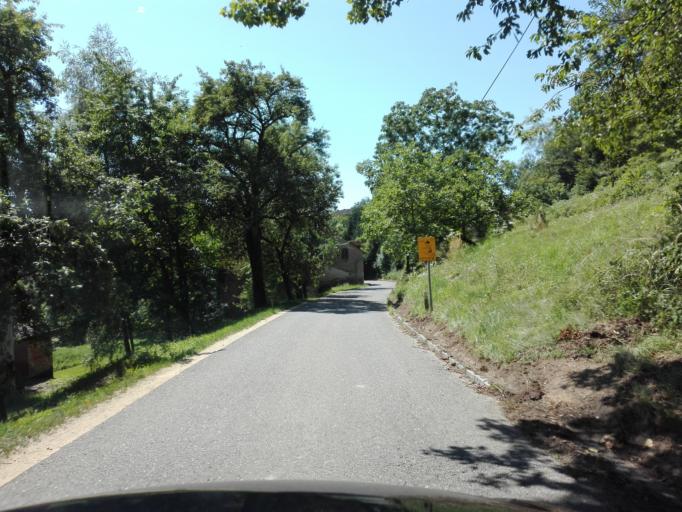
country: AT
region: Upper Austria
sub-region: Politischer Bezirk Urfahr-Umgebung
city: Gallneukirchen
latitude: 48.3261
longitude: 14.3970
